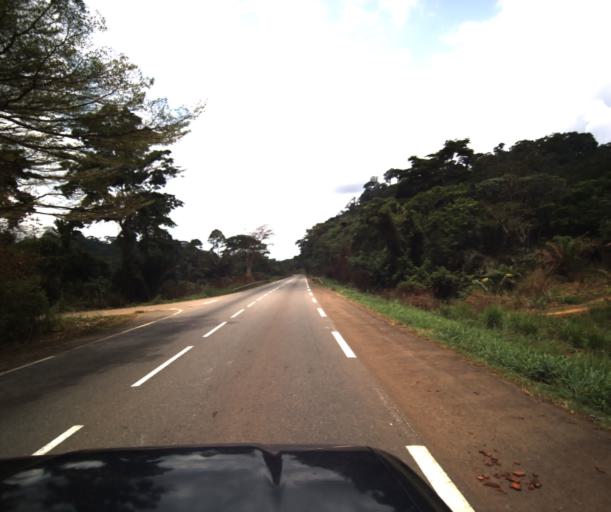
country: CM
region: Centre
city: Eseka
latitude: 3.8356
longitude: 10.9885
